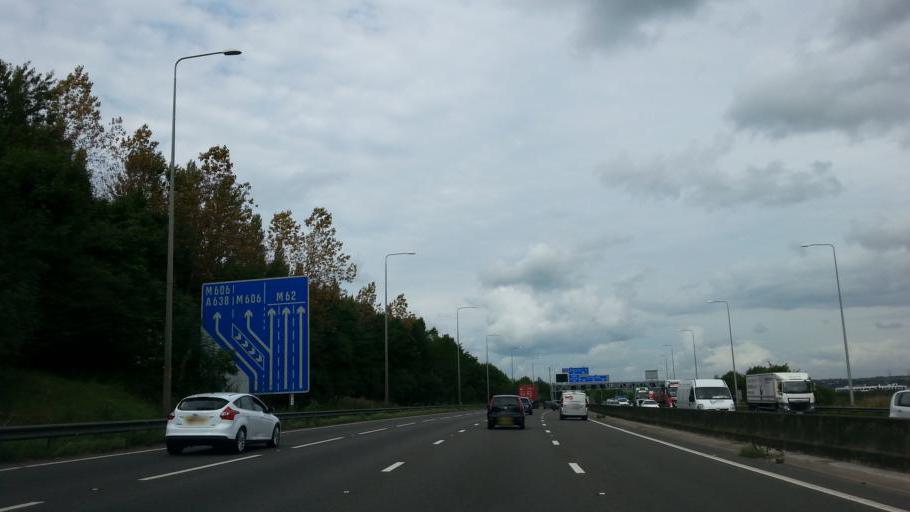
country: GB
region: England
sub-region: Kirklees
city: Cleckheaton
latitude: 53.7196
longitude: -1.7439
